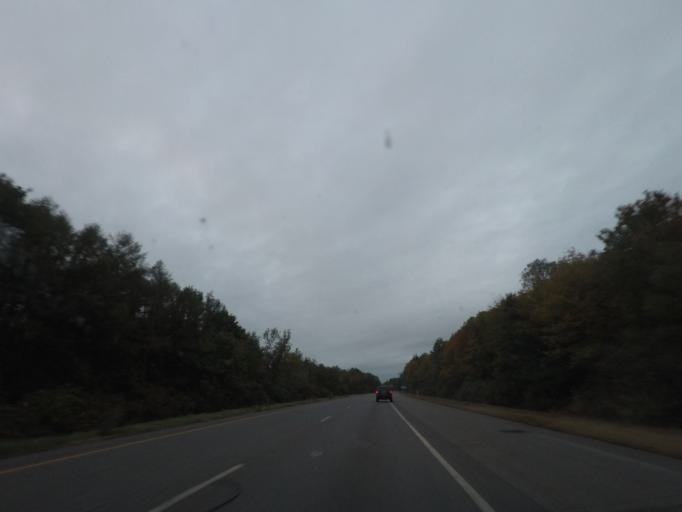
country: US
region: Massachusetts
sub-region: Worcester County
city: Oxford
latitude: 42.0931
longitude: -71.8631
